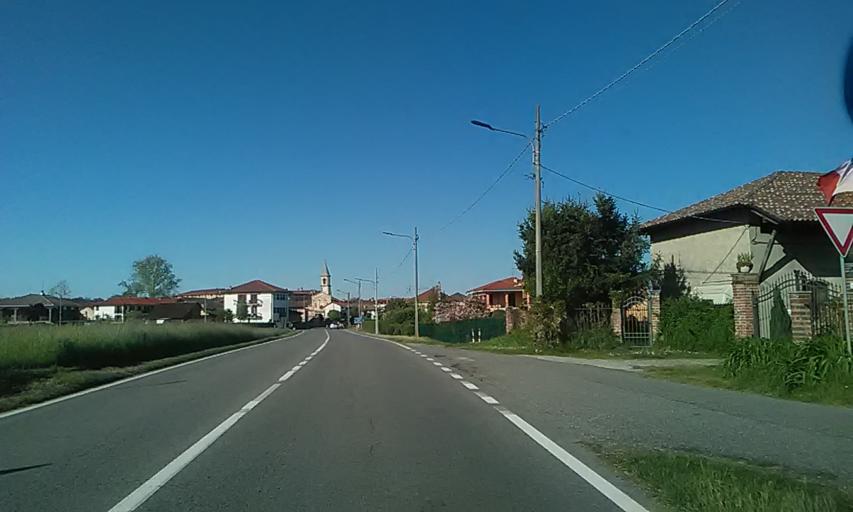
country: IT
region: Piedmont
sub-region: Provincia di Novara
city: Momo
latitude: 45.5844
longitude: 8.5816
